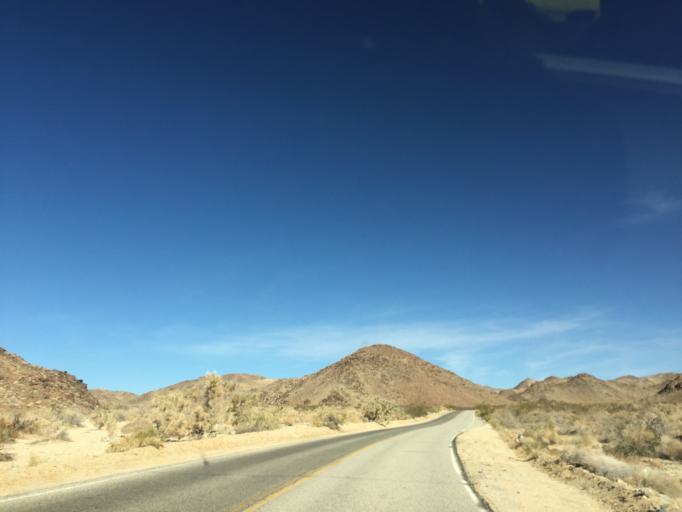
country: US
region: California
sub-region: San Bernardino County
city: Twentynine Palms
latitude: 33.9414
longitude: -115.9726
